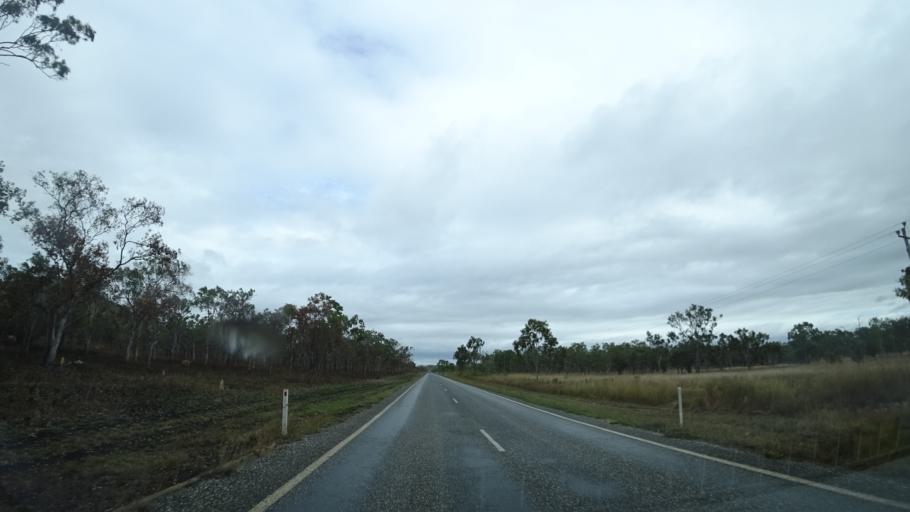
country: AU
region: Queensland
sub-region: Tablelands
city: Mareeba
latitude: -16.7553
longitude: 145.3427
